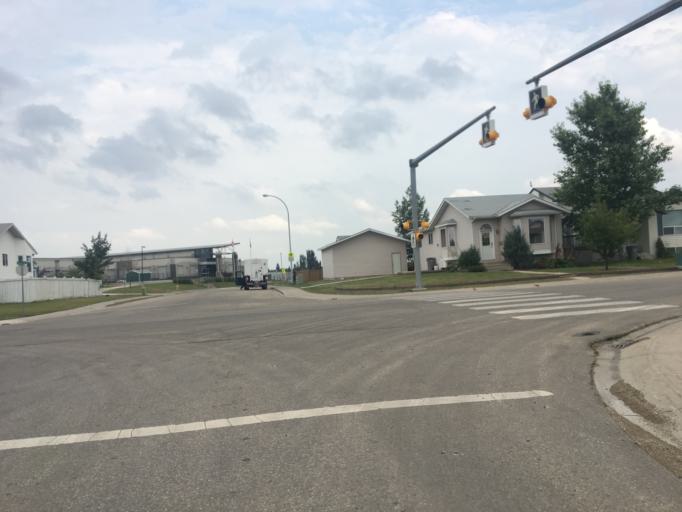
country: CA
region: Alberta
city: Grande Prairie
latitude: 55.1475
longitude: -118.8124
